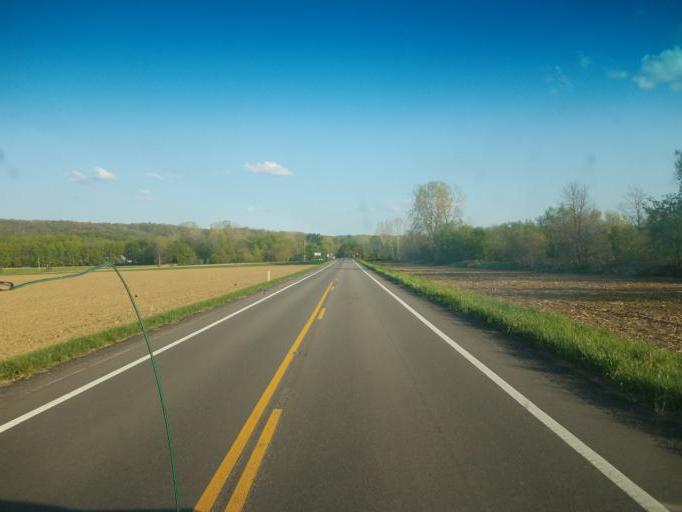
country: US
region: Ohio
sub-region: Holmes County
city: Millersburg
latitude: 40.5056
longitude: -81.9883
